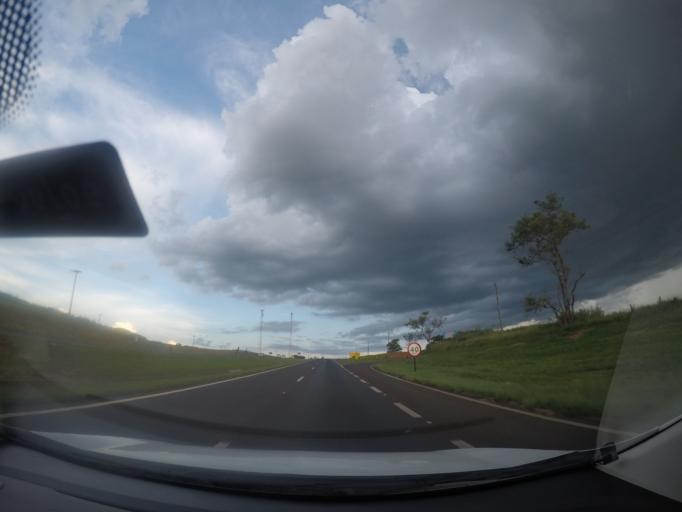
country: BR
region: Sao Paulo
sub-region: Ibate
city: Ibate
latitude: -21.9113
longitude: -48.0474
